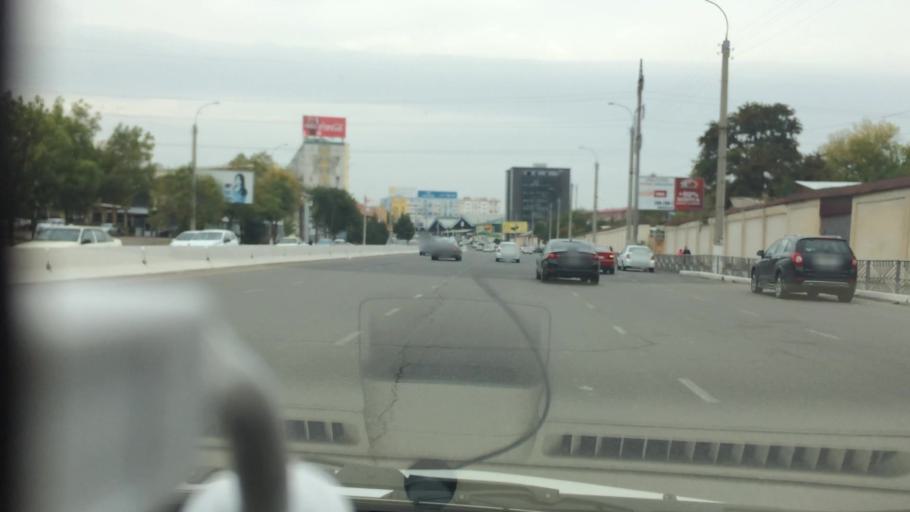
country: UZ
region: Toshkent
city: Salor
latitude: 41.3166
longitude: 69.3172
